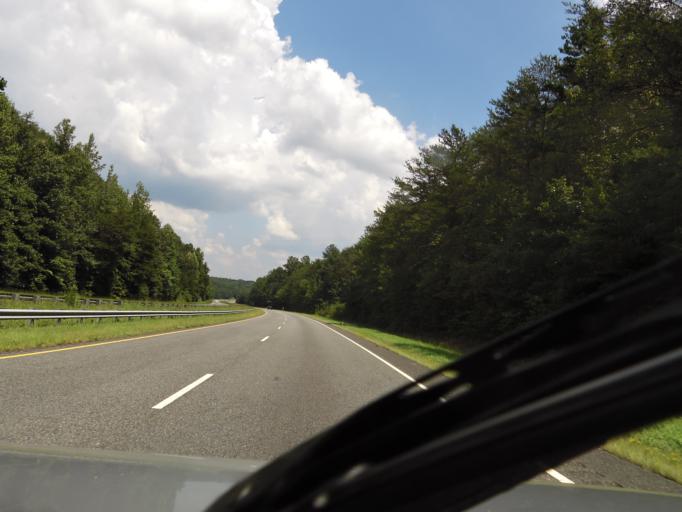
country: US
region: North Carolina
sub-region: Polk County
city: Columbus
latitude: 35.2611
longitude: -82.1763
